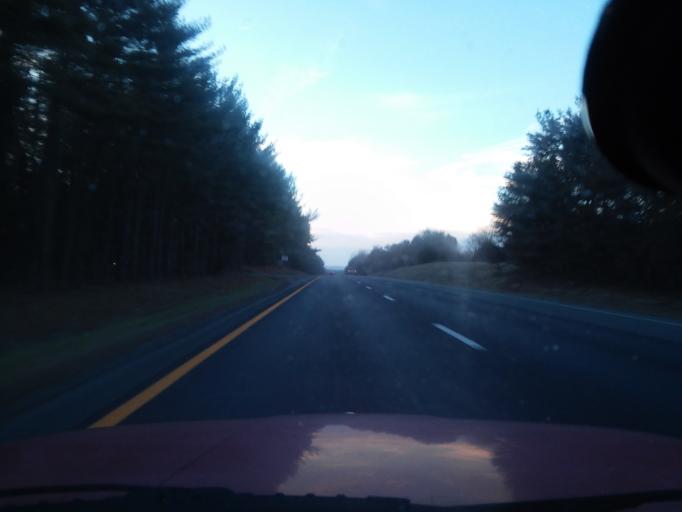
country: US
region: Virginia
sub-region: Louisa County
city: Louisa
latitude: 37.9432
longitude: -78.1150
